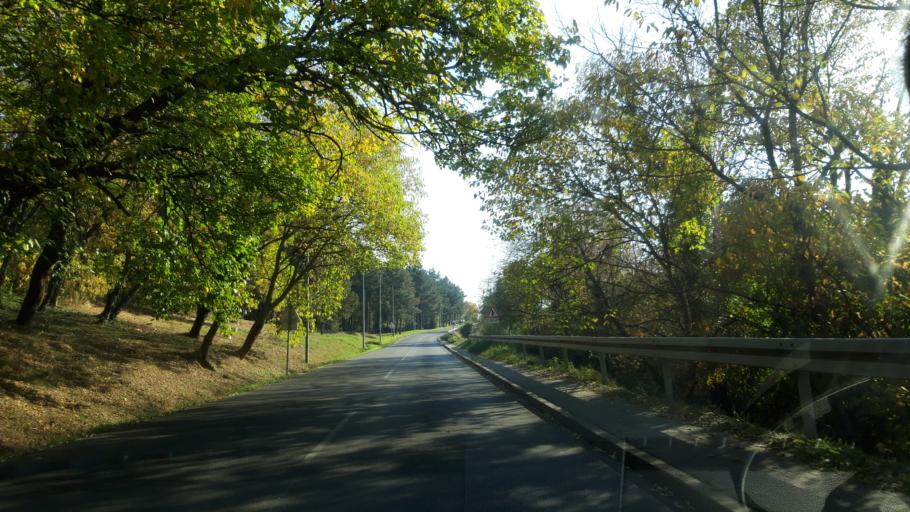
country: RS
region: Autonomna Pokrajina Vojvodina
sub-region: Juznobacki Okrug
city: Petrovaradin
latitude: 45.2449
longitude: 19.8664
